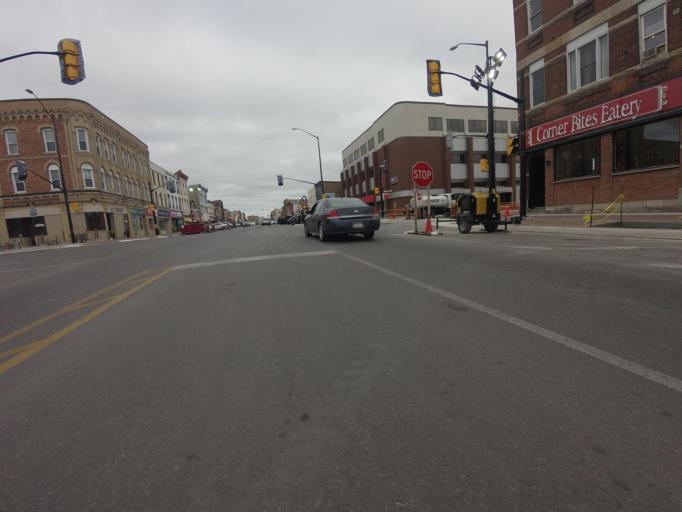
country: CA
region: Ontario
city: Omemee
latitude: 44.3544
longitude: -78.7396
